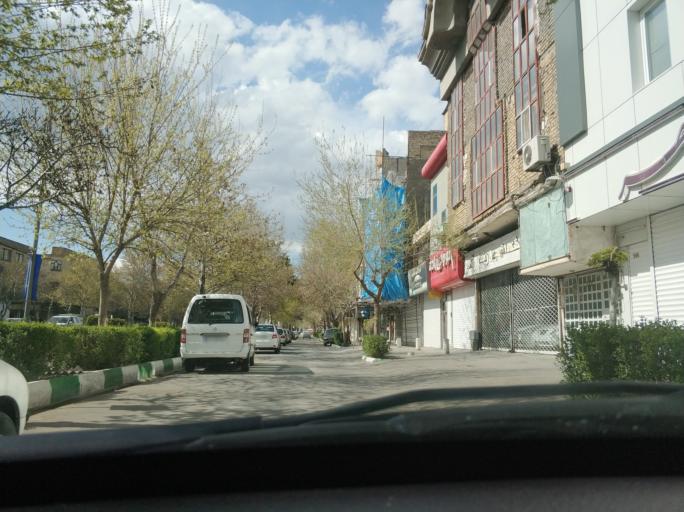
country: IR
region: Razavi Khorasan
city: Mashhad
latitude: 36.2726
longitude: 59.5944
